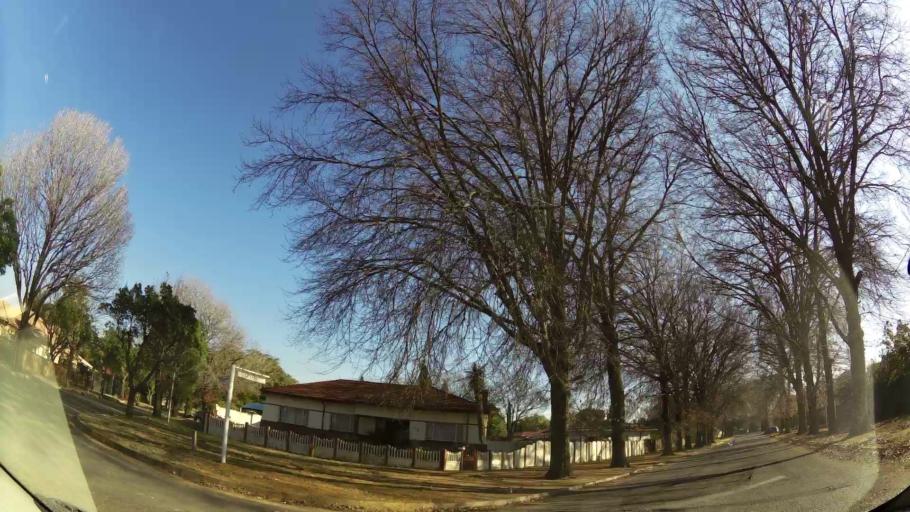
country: ZA
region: Gauteng
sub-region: Ekurhuleni Metropolitan Municipality
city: Benoni
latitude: -26.1689
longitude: 28.3135
